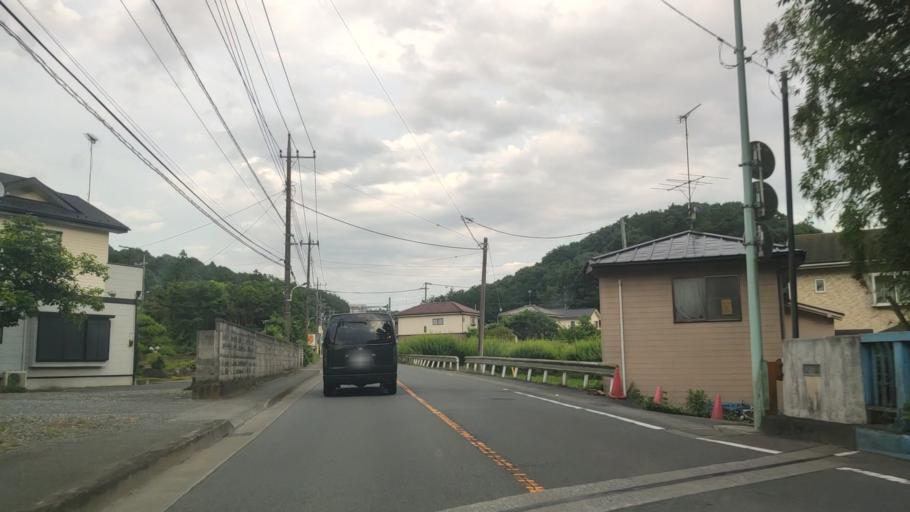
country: JP
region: Saitama
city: Hanno
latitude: 35.8209
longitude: 139.2913
